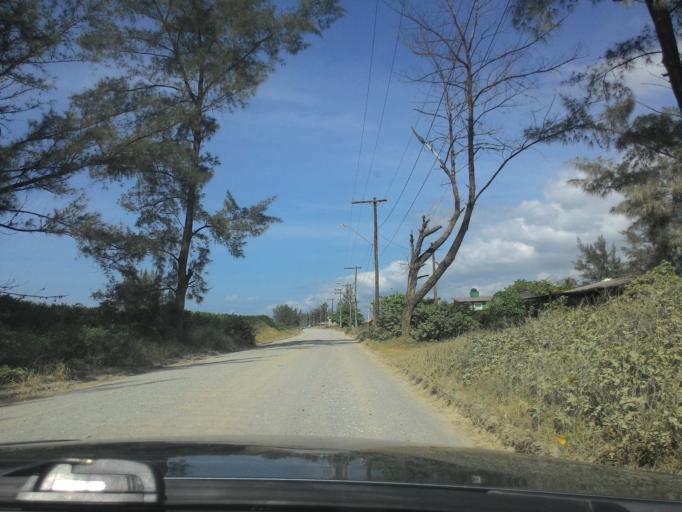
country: BR
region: Sao Paulo
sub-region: Iguape
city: Iguape
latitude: -24.8361
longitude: -47.6758
